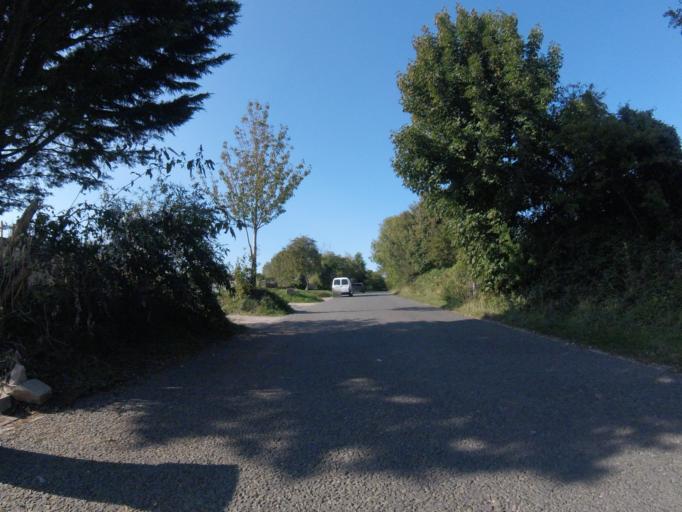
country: GB
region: England
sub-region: Brighton and Hove
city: Hove
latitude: 50.8708
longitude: -0.1575
